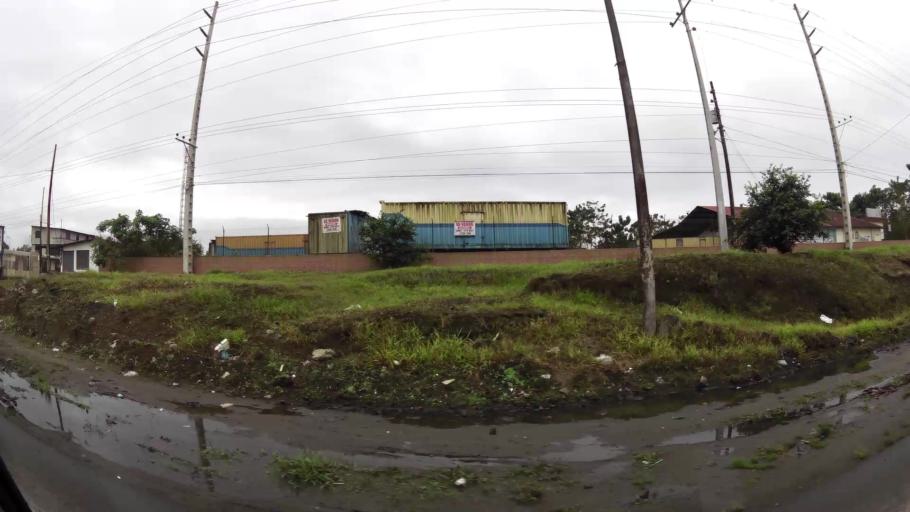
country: EC
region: Santo Domingo de los Tsachilas
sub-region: Canton Santo Domingo de los Colorados
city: Santo Domingo de los Colorados
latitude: -0.2607
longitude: -79.2025
